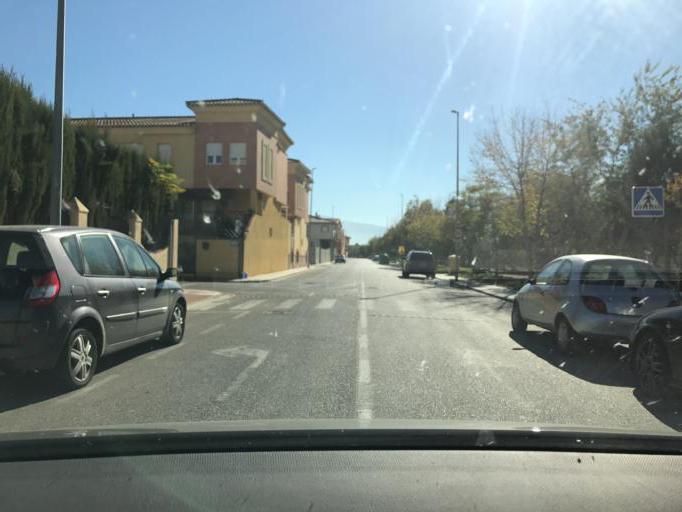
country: ES
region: Andalusia
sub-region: Provincia de Granada
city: Maracena
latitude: 37.2084
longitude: -3.6460
